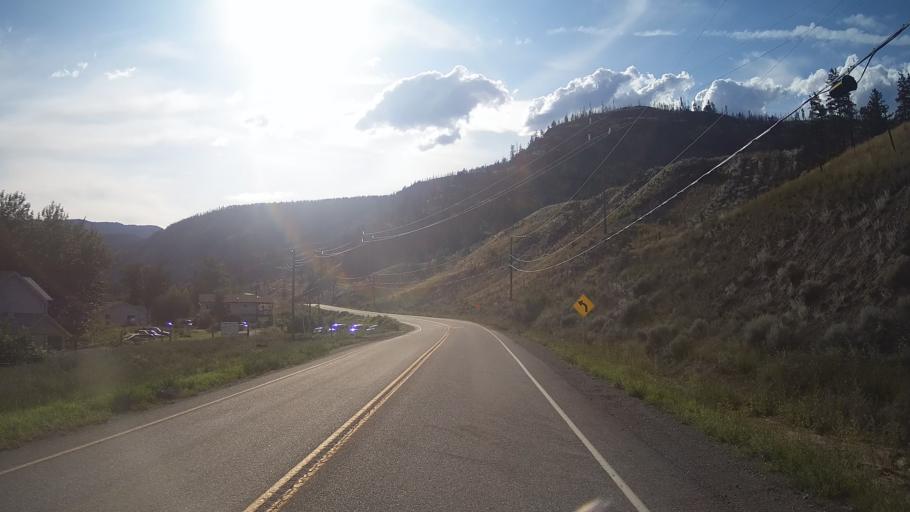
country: CA
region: British Columbia
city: Cache Creek
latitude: 50.8846
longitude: -121.4788
